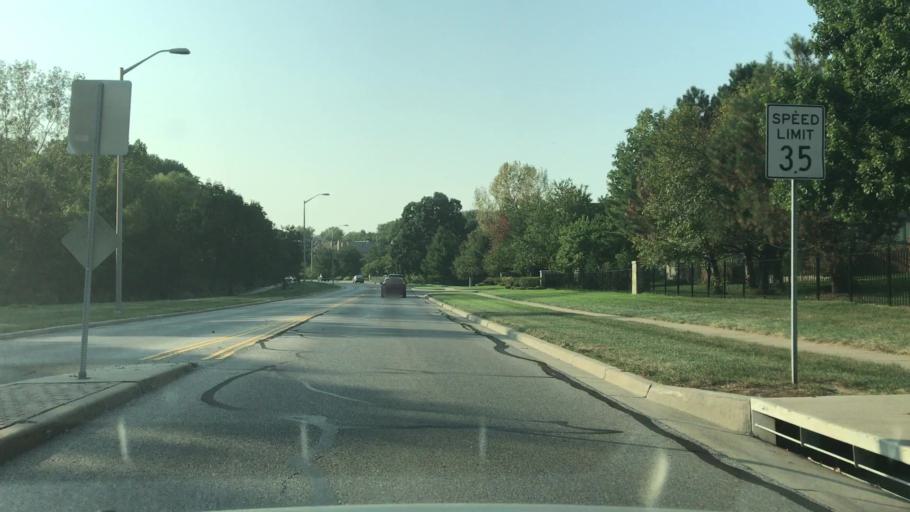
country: US
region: Kansas
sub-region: Johnson County
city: Lenexa
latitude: 38.9938
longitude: -94.7379
